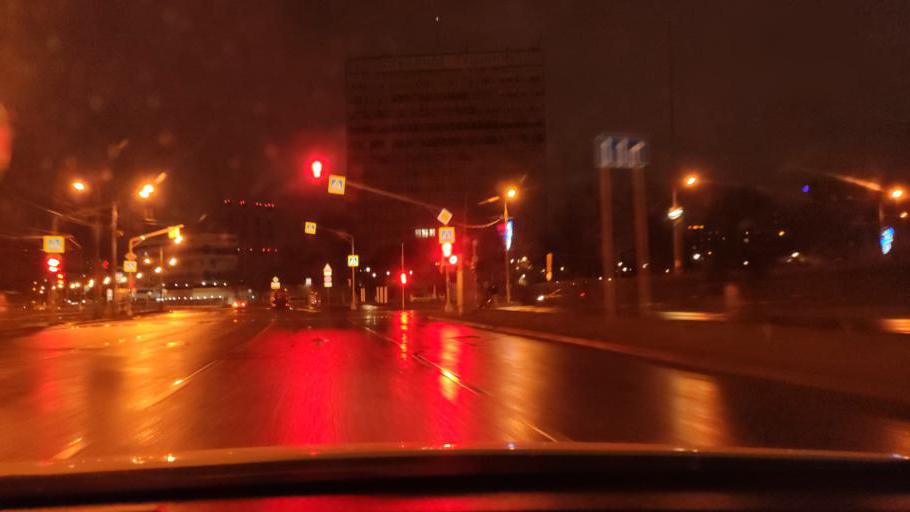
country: RU
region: Moscow
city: Khimki
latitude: 55.8549
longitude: 37.4378
